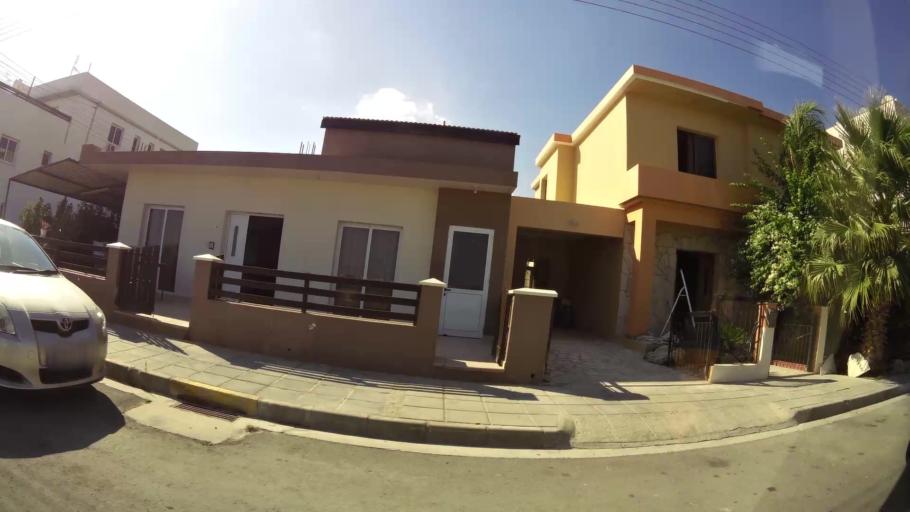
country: CY
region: Larnaka
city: Livadia
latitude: 34.9452
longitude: 33.6369
